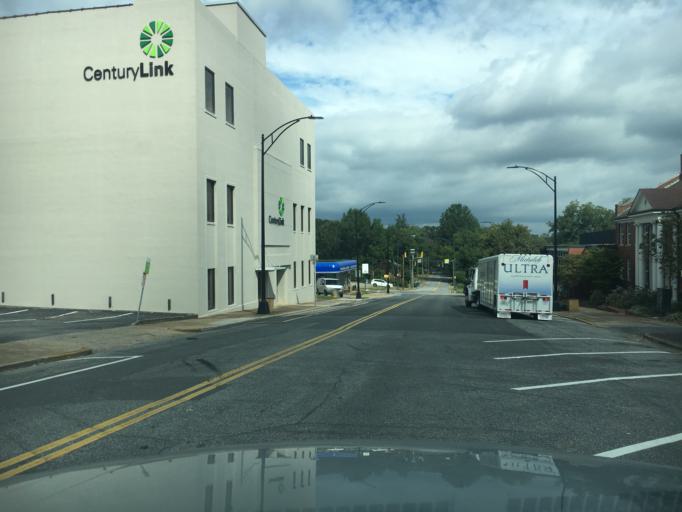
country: US
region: North Carolina
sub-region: Catawba County
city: Hickory
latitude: 35.7335
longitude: -81.3422
